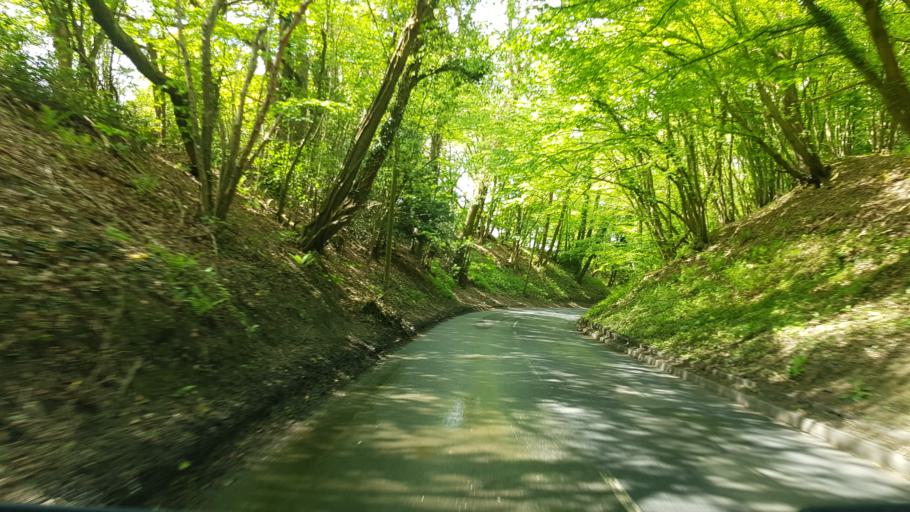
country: GB
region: England
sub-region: East Sussex
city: Robertsbridge
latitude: 51.0311
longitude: 0.4570
